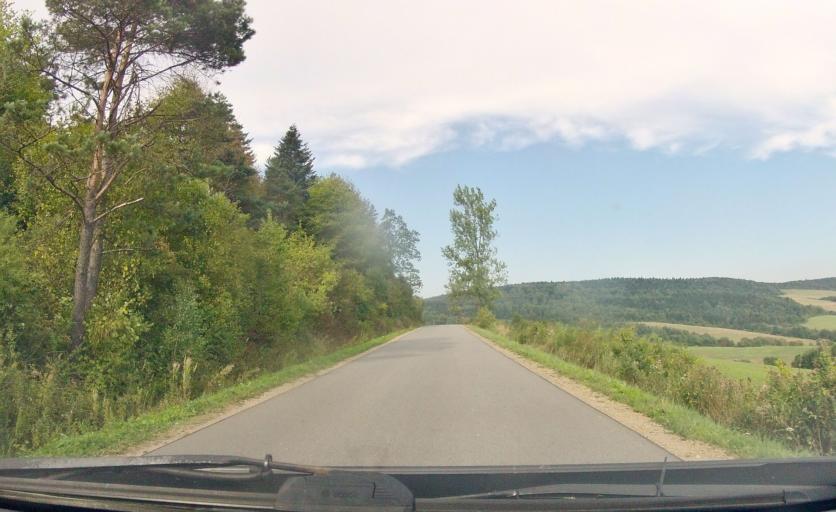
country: PL
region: Subcarpathian Voivodeship
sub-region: Powiat krosnienski
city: Dukla
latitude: 49.5061
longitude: 21.6256
